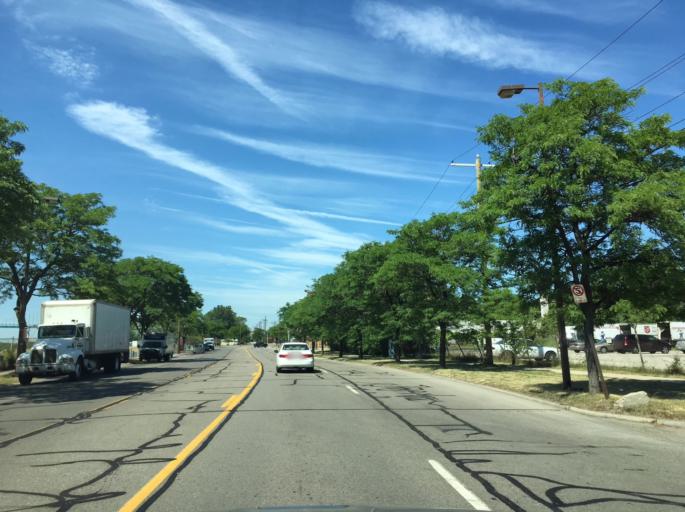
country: US
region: Michigan
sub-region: Wayne County
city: Detroit
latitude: 42.3225
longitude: -83.0631
